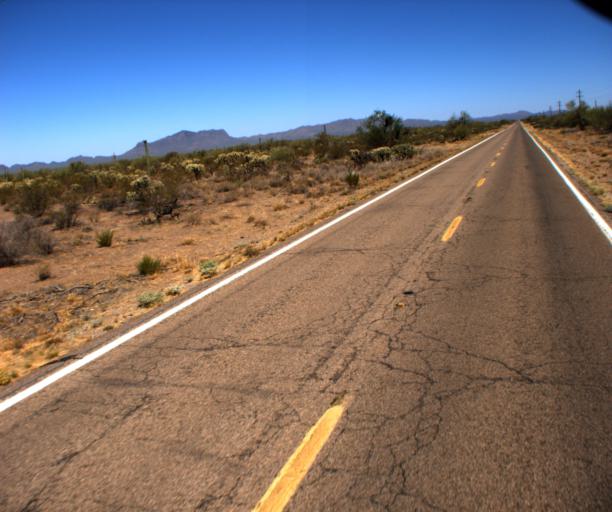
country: US
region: Arizona
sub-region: Pima County
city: Sells
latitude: 31.9967
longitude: -111.9826
